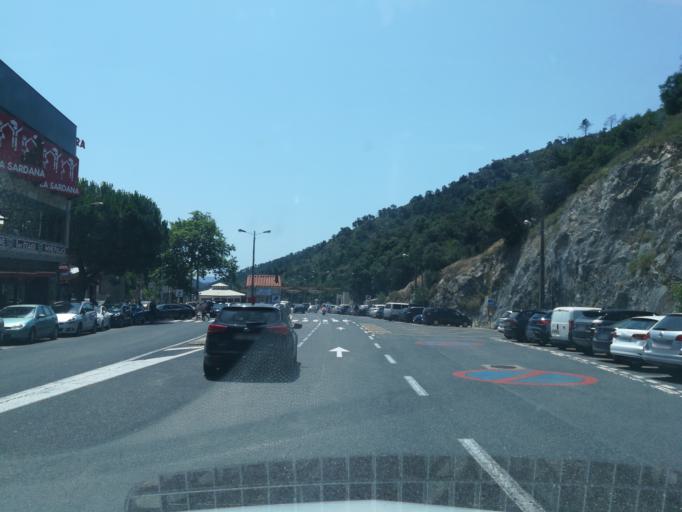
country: ES
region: Catalonia
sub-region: Provincia de Girona
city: la Jonquera
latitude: 42.4606
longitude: 2.8641
